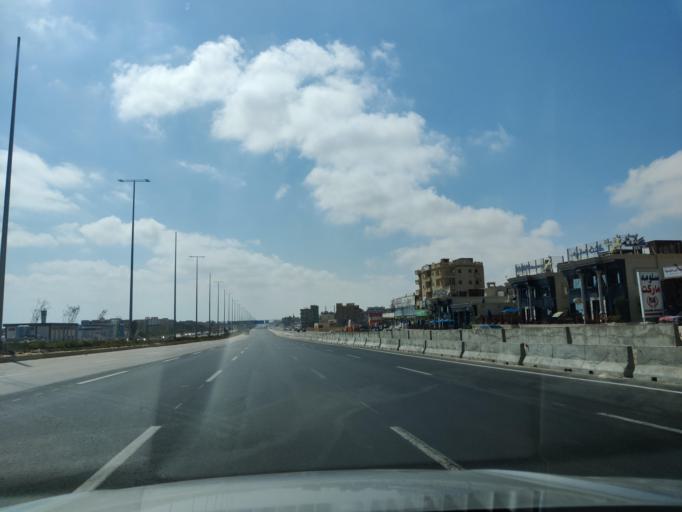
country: EG
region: Muhafazat Matruh
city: Al `Alamayn
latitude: 30.9729
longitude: 28.7352
